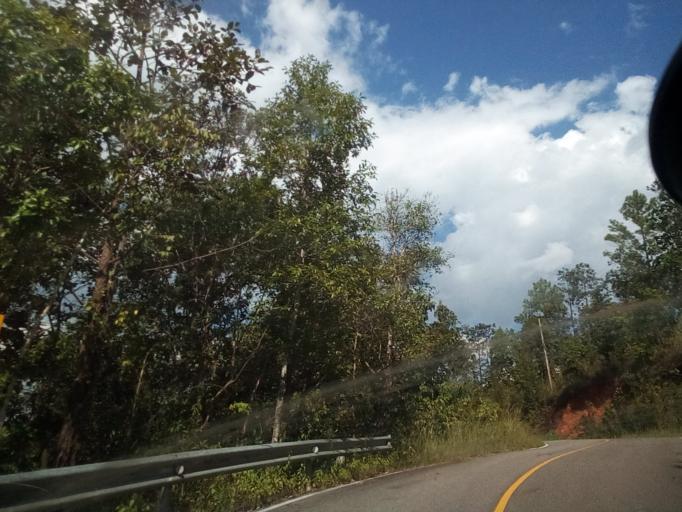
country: TH
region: Chiang Mai
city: Samoeng
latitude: 18.8769
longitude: 98.6806
